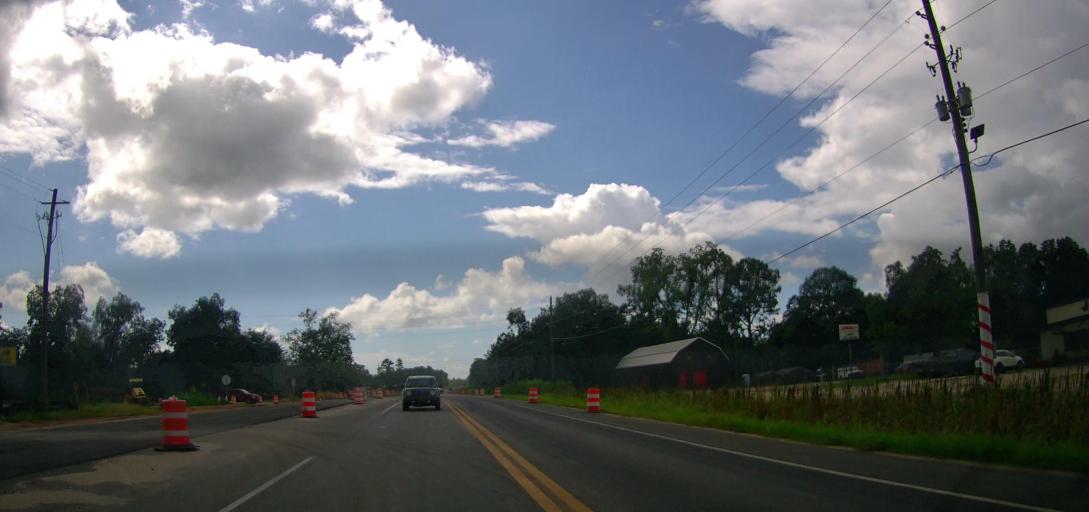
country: US
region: Georgia
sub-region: Coffee County
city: Douglas
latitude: 31.5212
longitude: -82.8926
